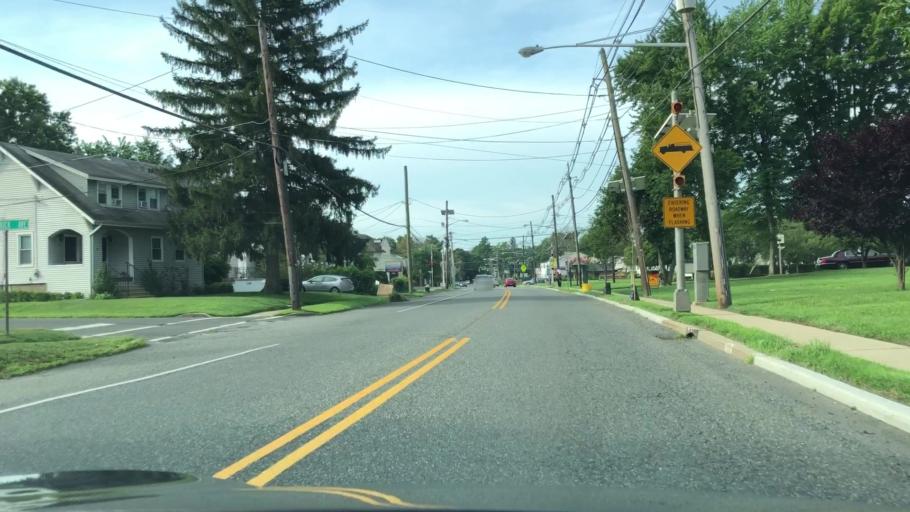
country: US
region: New Jersey
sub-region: Mercer County
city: Lawrenceville
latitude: 40.2669
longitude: -74.7405
